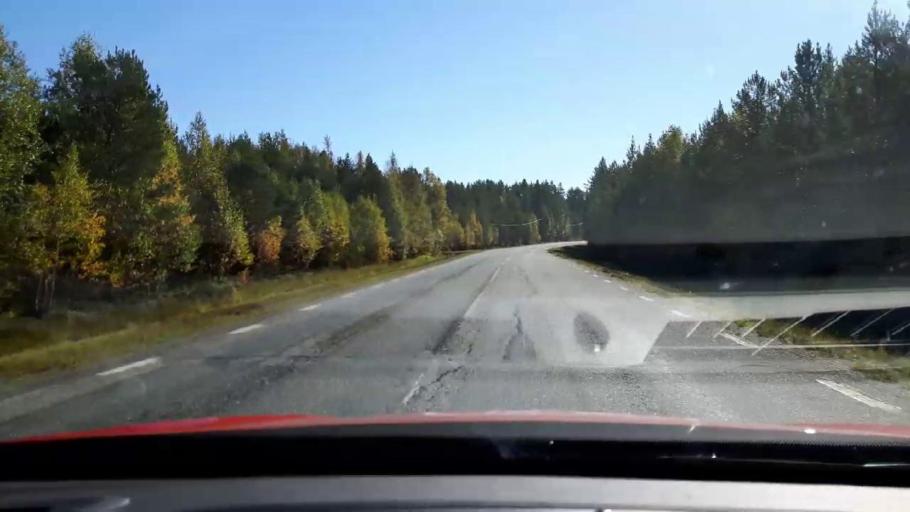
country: SE
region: Jaemtland
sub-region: Harjedalens Kommun
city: Sveg
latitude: 62.3351
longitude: 14.0515
